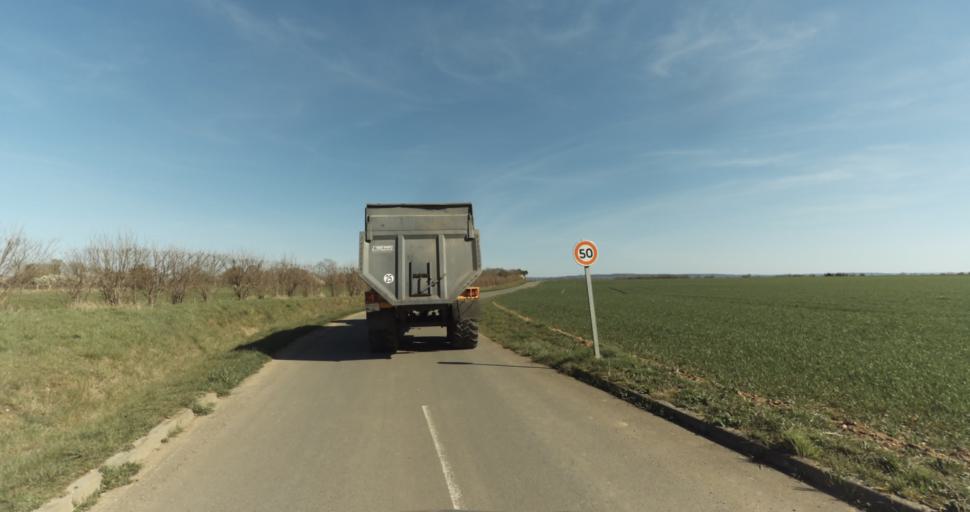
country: FR
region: Lower Normandy
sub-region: Departement du Calvados
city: Canon
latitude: 49.0498
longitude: -0.0643
